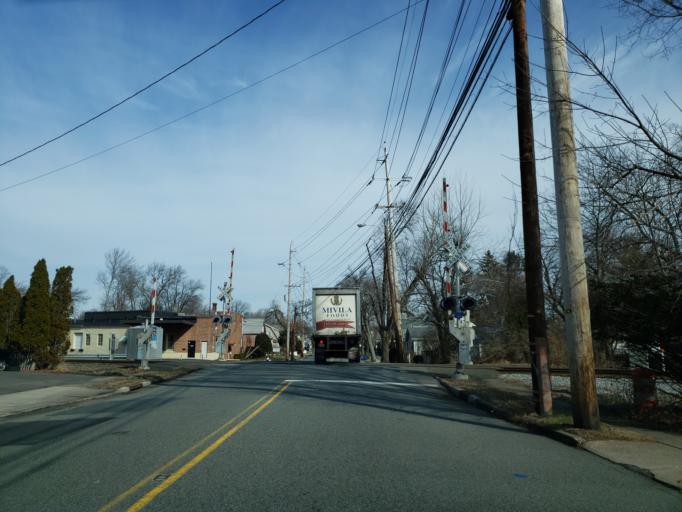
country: US
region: New Jersey
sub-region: Passaic County
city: Singac
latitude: 40.8762
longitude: -74.2313
